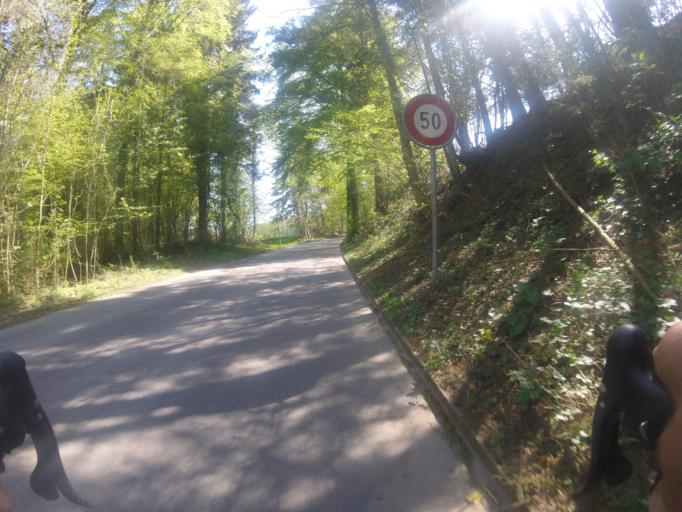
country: CH
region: Bern
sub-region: Bern-Mittelland District
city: Laupen
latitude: 46.9047
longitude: 7.2441
